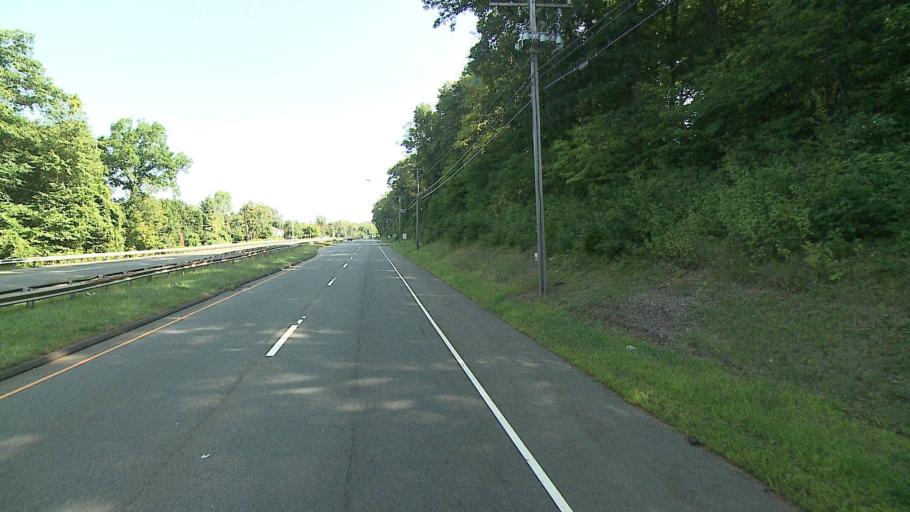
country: US
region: Connecticut
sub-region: New Haven County
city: Meriden
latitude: 41.5762
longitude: -72.7685
